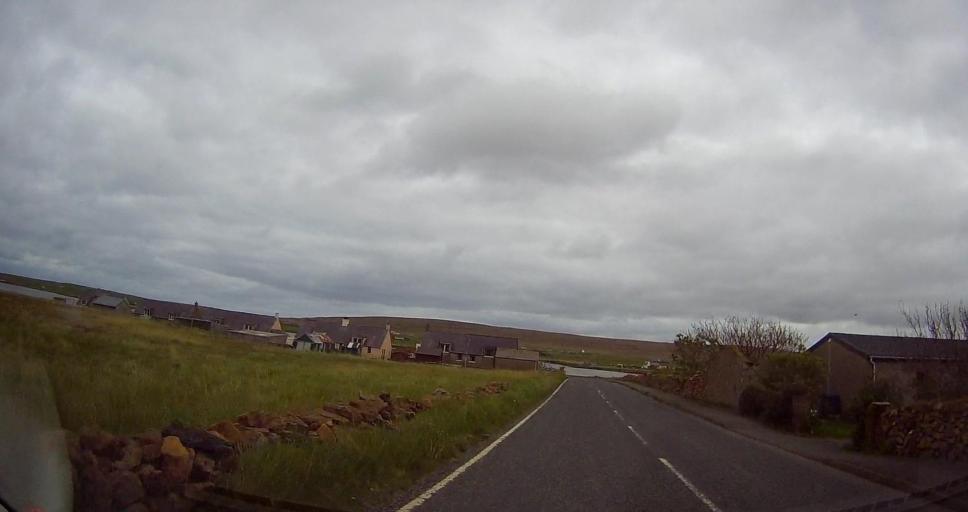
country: GB
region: Scotland
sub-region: Shetland Islands
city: Shetland
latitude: 60.7598
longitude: -0.8588
